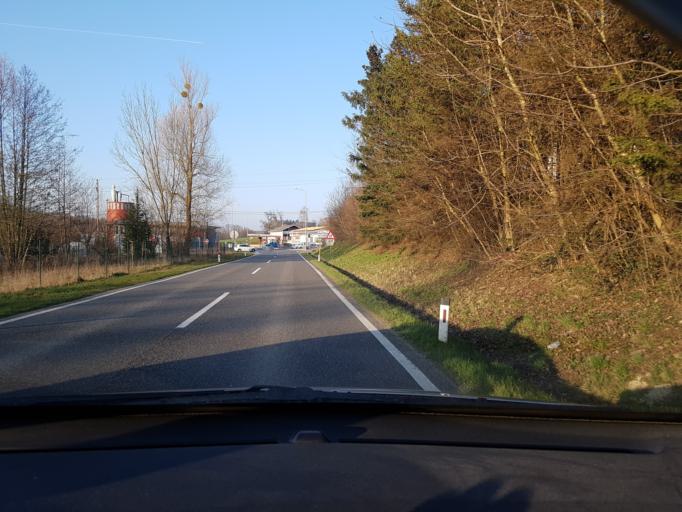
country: AT
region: Upper Austria
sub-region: Politischer Bezirk Linz-Land
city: Sankt Florian
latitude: 48.1628
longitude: 14.3380
